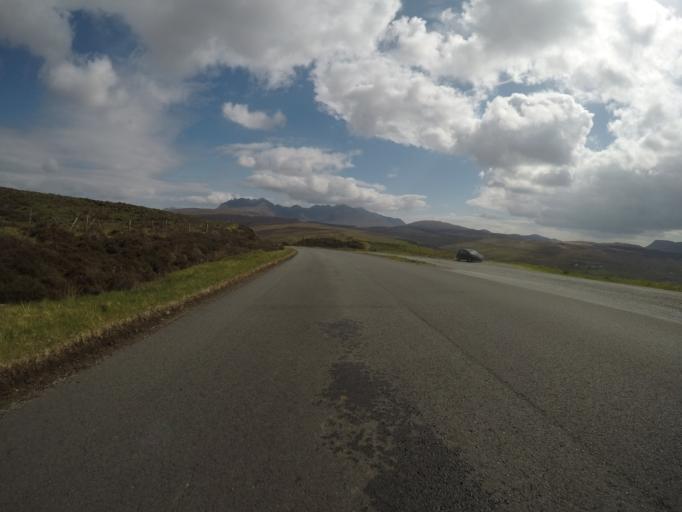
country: GB
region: Scotland
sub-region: Highland
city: Isle of Skye
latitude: 57.3064
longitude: -6.3149
